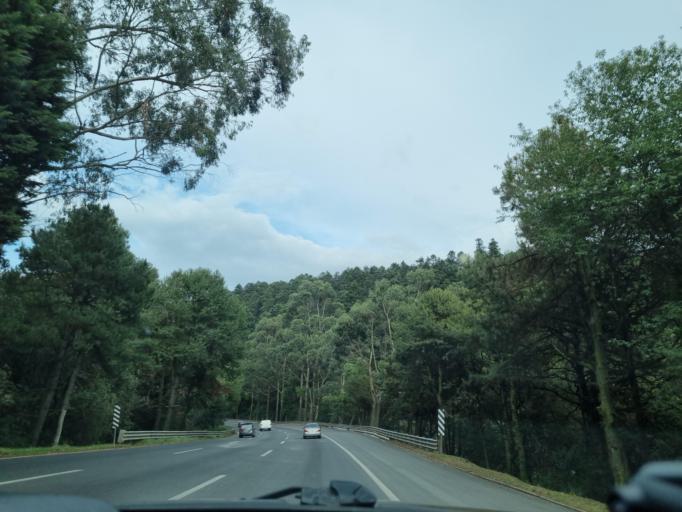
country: MX
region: Morelos
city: San Jeronimo Acazulco
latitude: 19.2922
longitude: -99.4218
